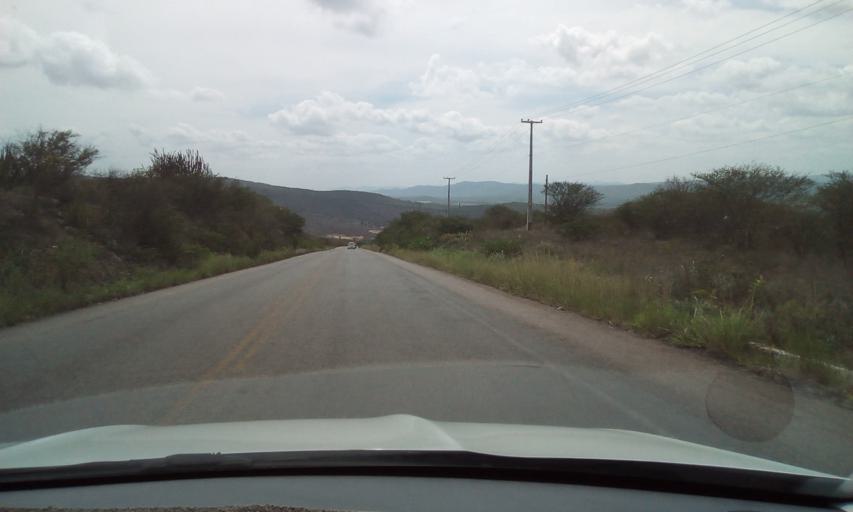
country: BR
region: Pernambuco
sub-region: Bezerros
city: Bezerros
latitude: -8.2738
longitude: -35.7461
